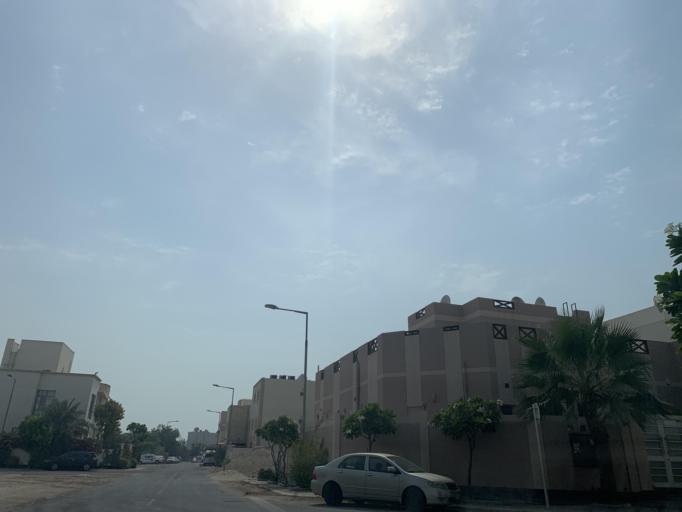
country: BH
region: Manama
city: Jidd Hafs
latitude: 26.2089
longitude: 50.4894
